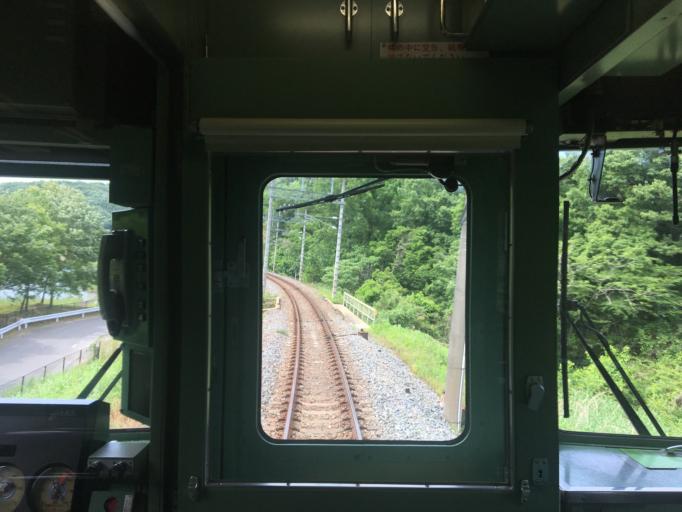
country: JP
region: Saitama
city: Yorii
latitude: 36.0935
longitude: 139.2364
